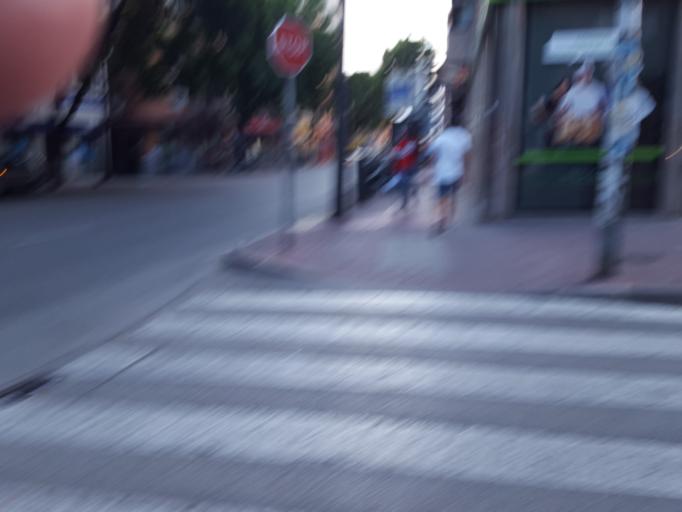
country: ES
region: Murcia
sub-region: Murcia
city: Murcia
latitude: 37.9774
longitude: -1.1322
